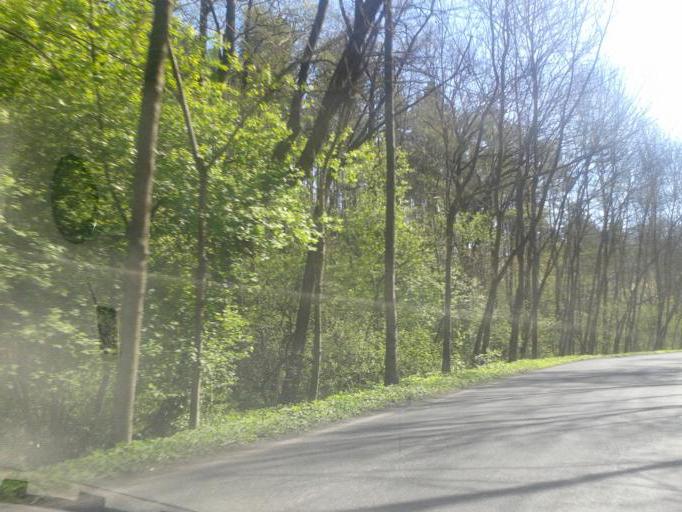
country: CZ
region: Central Bohemia
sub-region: Okres Beroun
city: Kraluv Dvur
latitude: 49.9377
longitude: 14.0440
